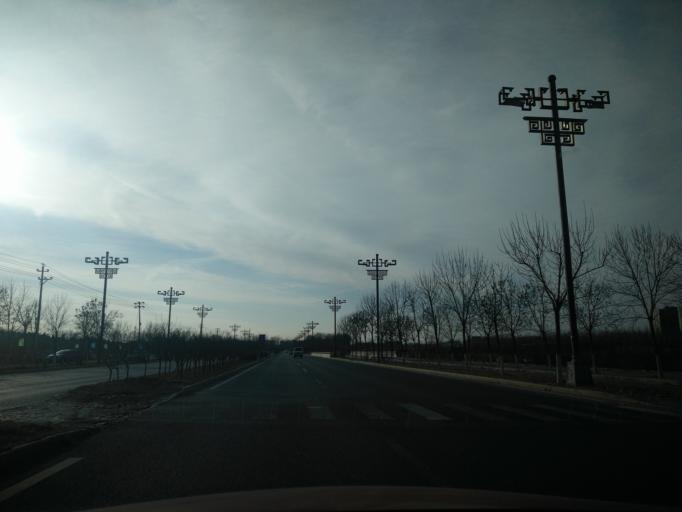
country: CN
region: Beijing
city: Jiugong
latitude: 39.7869
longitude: 116.4567
